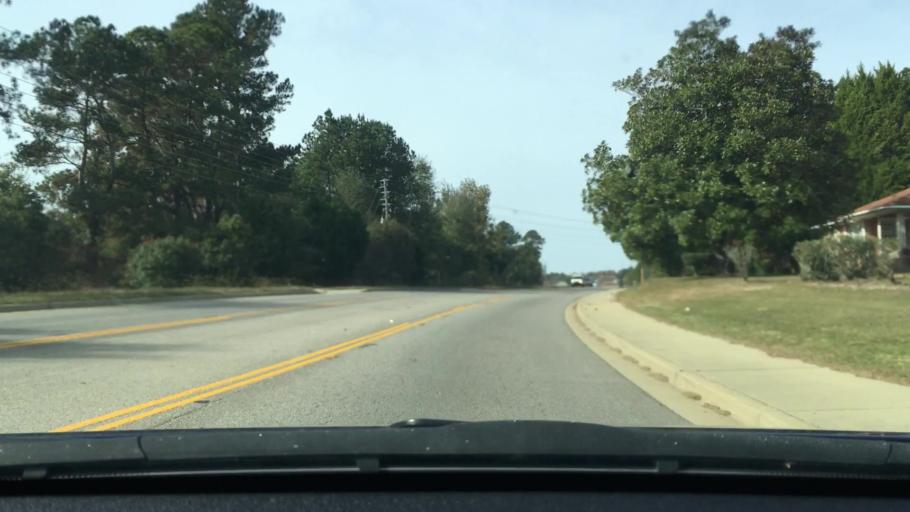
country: US
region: South Carolina
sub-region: Sumter County
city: Cane Savannah
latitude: 33.9261
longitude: -80.4070
